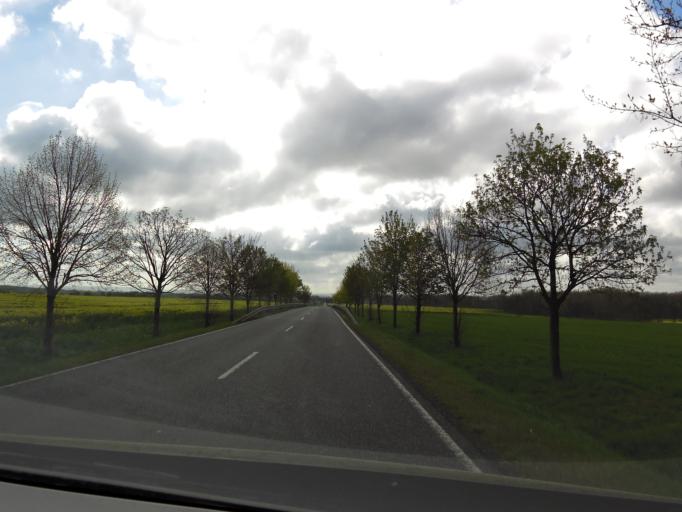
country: DE
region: Thuringia
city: Wandersleben
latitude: 50.9092
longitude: 10.8280
